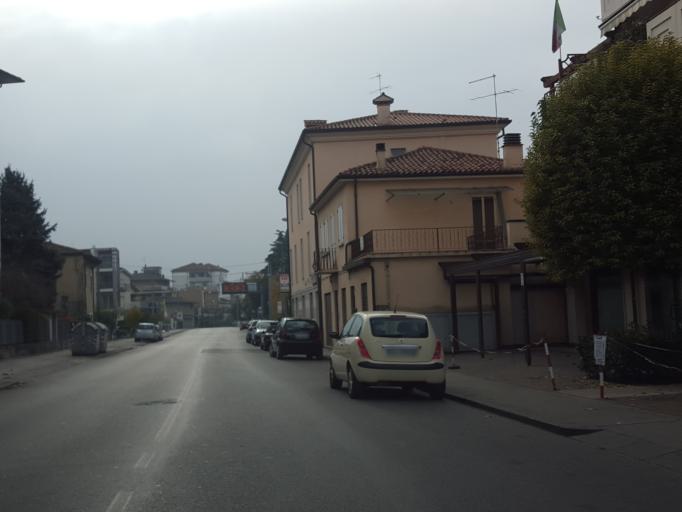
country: IT
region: Veneto
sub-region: Provincia di Vicenza
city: Vicenza
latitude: 45.5579
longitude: 11.5584
